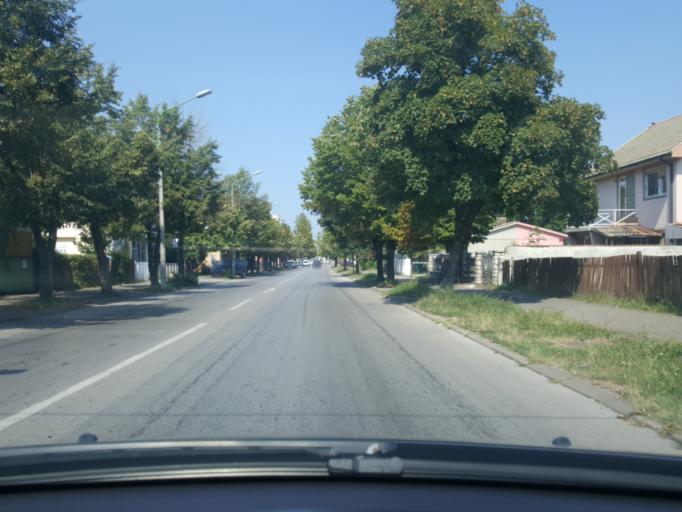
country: RS
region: Central Serbia
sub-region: Macvanski Okrug
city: Sabac
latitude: 44.7466
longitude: 19.7011
